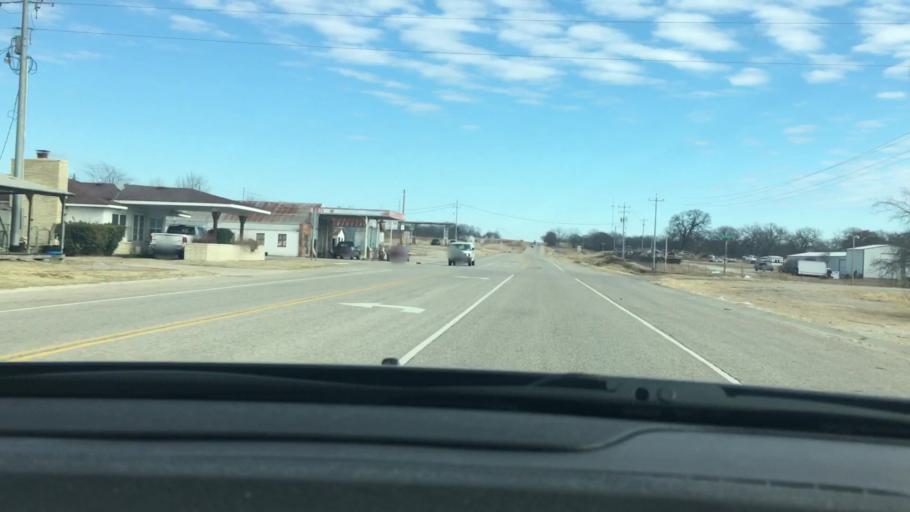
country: US
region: Oklahoma
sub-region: Garvin County
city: Stratford
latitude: 34.7967
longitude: -96.8630
